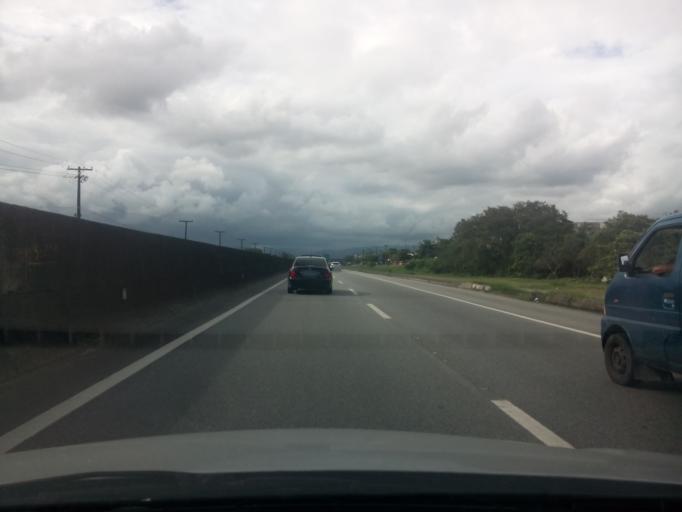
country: BR
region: Sao Paulo
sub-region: Guaruja
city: Guaruja
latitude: -23.9765
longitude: -46.2677
